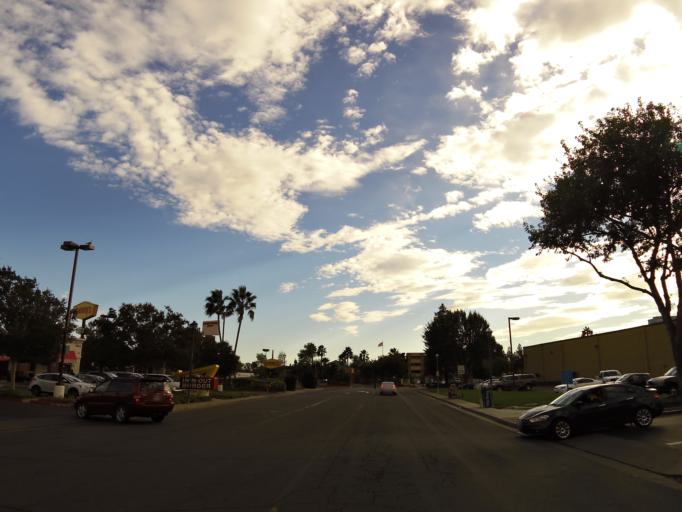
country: US
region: California
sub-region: Solano County
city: Fairfield
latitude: 38.2579
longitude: -122.0652
